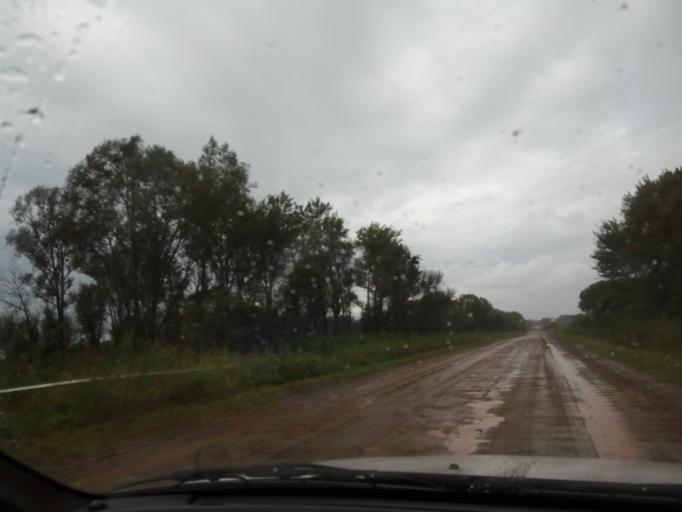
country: RU
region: Primorskiy
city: Lazo
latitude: 45.8484
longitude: 133.6454
